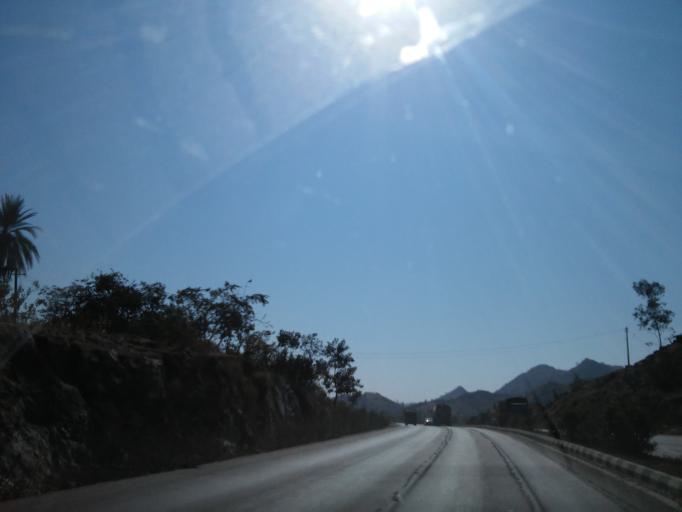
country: IN
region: Rajasthan
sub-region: Dungarpur
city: Dungarpur
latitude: 24.1393
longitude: 73.6942
